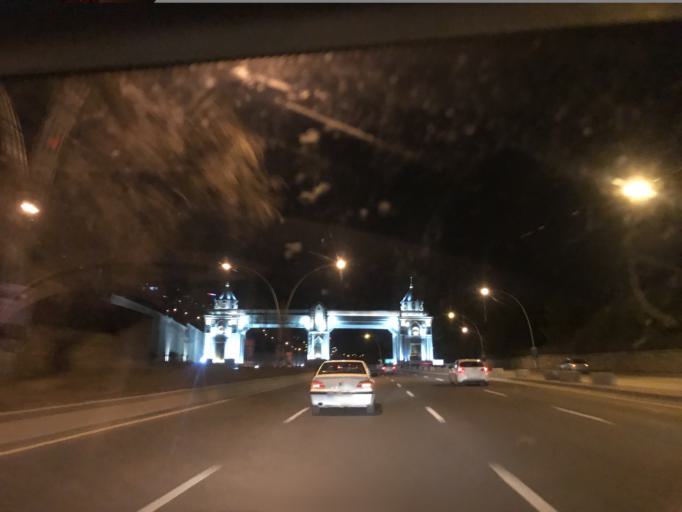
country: TR
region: Ankara
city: Ankara
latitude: 39.8663
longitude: 32.8103
